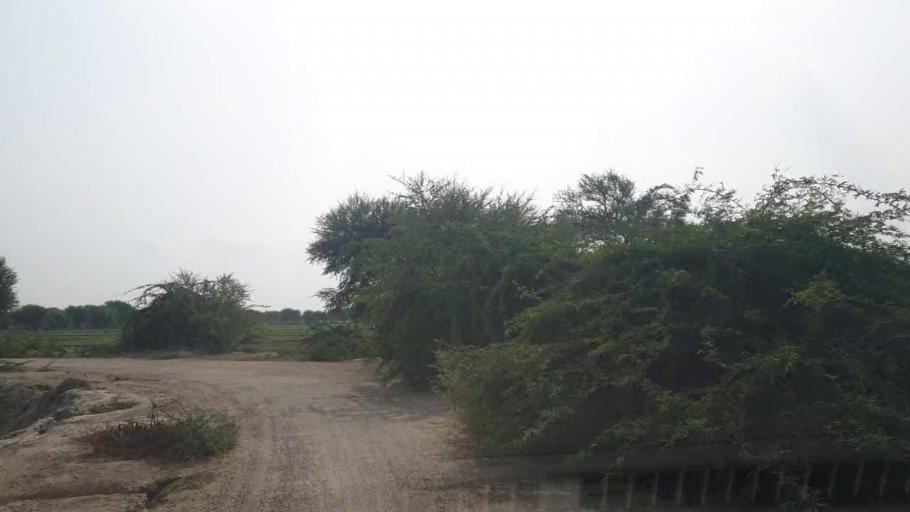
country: PK
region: Sindh
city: Badin
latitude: 24.5478
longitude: 68.6876
